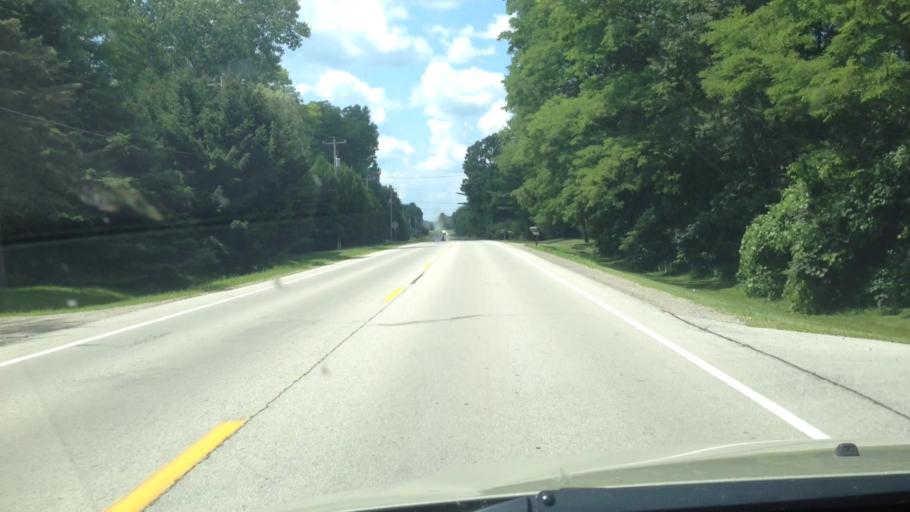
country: US
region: Wisconsin
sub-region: Brown County
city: Suamico
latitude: 44.6391
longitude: -88.0721
